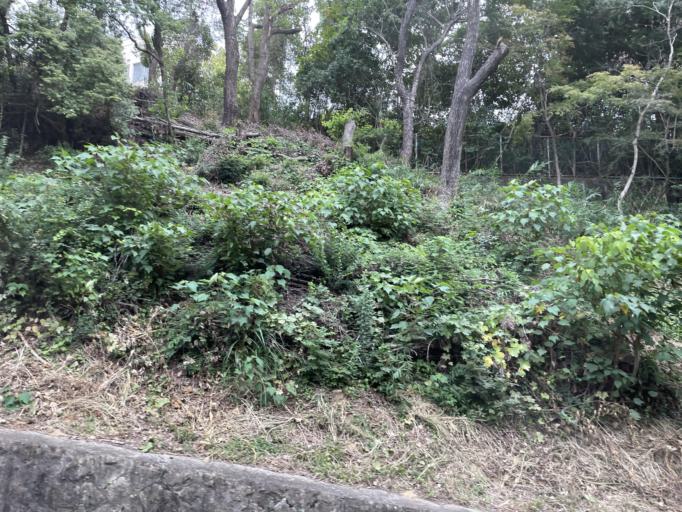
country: JP
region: Osaka
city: Ikeda
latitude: 34.8864
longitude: 135.4149
